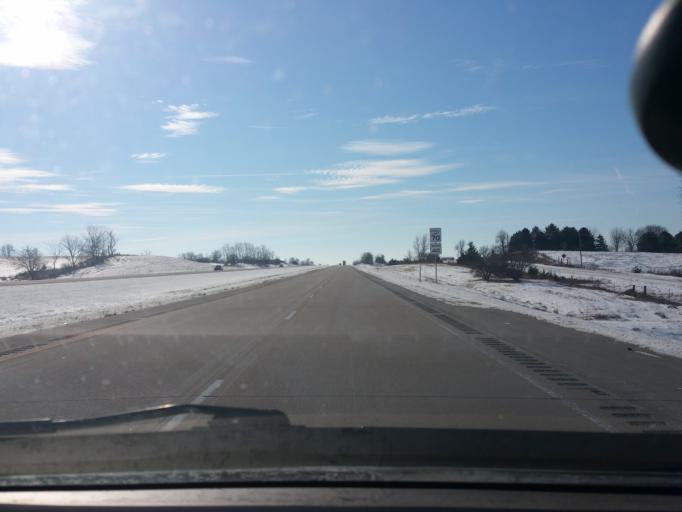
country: US
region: Iowa
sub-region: Decatur County
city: Leon
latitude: 40.8604
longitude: -93.8035
